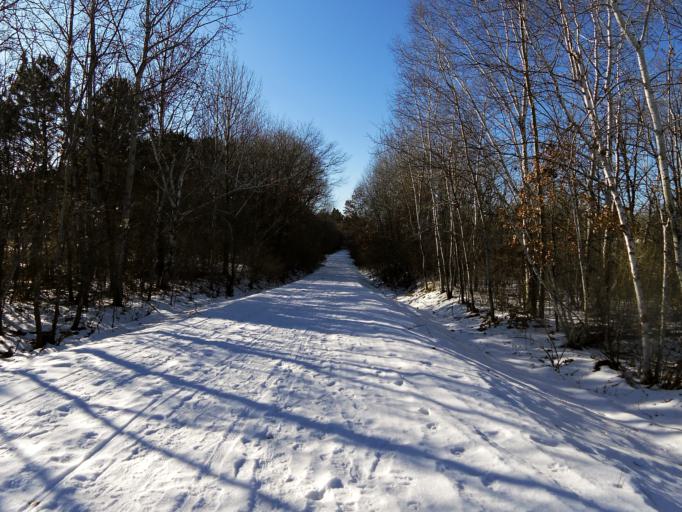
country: US
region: Minnesota
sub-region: Washington County
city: Grant
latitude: 45.0722
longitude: -92.8643
